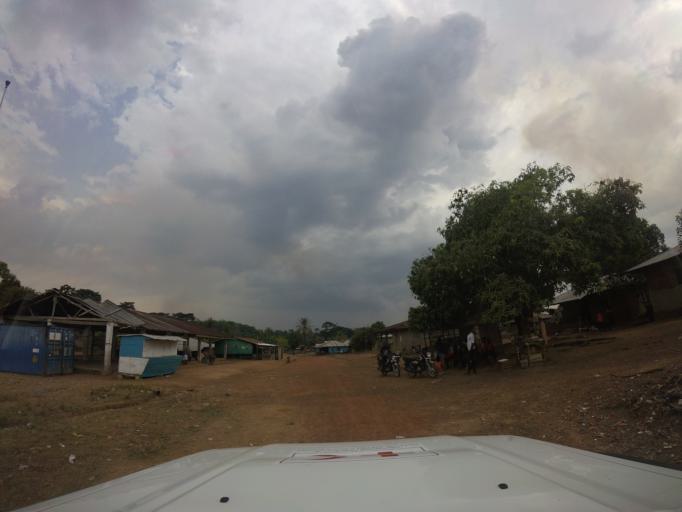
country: SL
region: Southern Province
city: Zimmi
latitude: 7.1372
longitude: -11.2828
